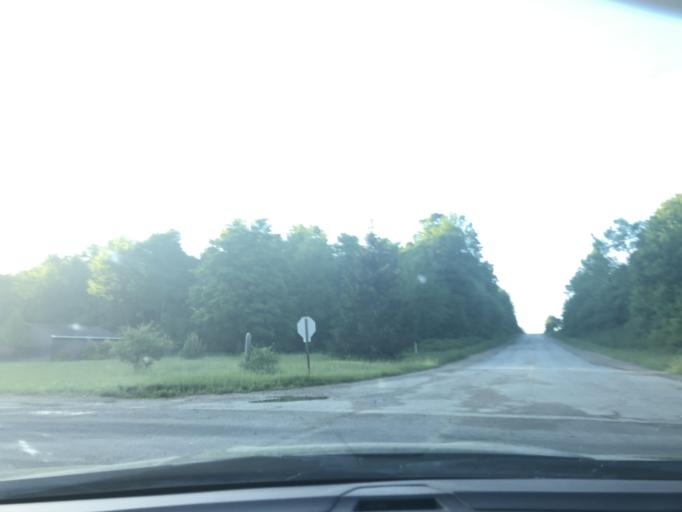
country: US
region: Michigan
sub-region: Missaukee County
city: Lake City
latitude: 44.4663
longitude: -85.0742
